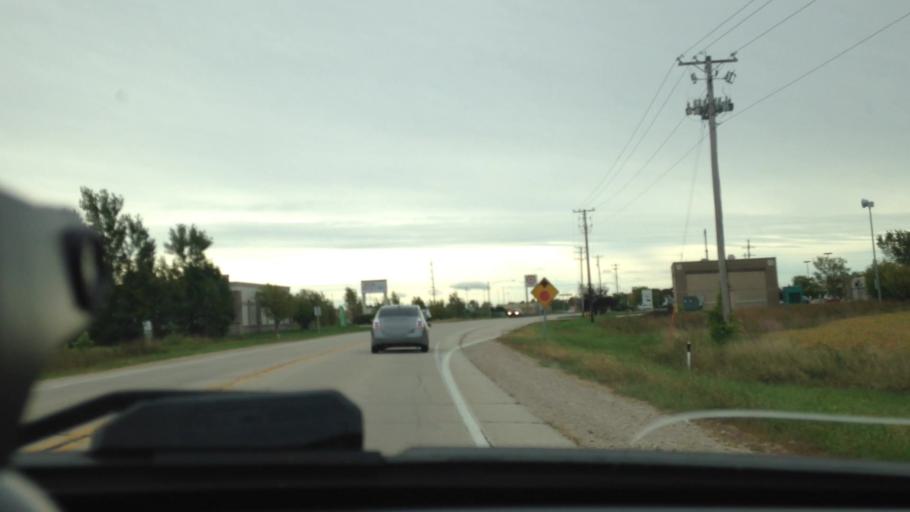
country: US
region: Wisconsin
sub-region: Fond du Lac County
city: North Fond du Lac
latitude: 43.7944
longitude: -88.4869
